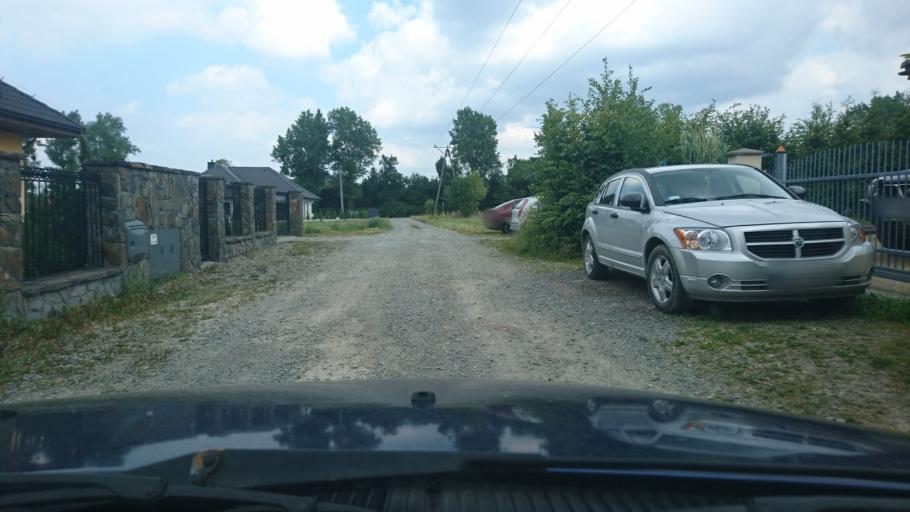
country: PL
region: Silesian Voivodeship
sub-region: Powiat bielski
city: Jaworze
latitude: 49.8045
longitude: 18.9733
